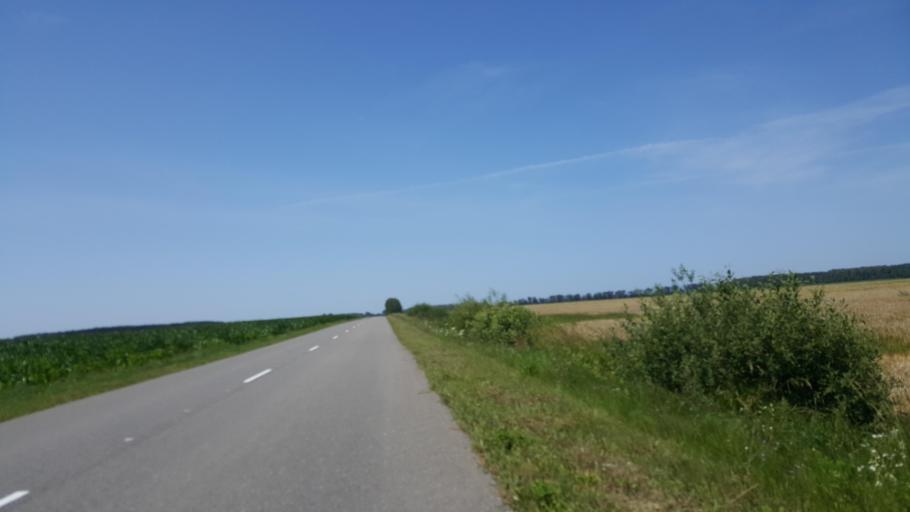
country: BY
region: Brest
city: Kamyanyets
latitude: 52.3766
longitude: 23.6159
